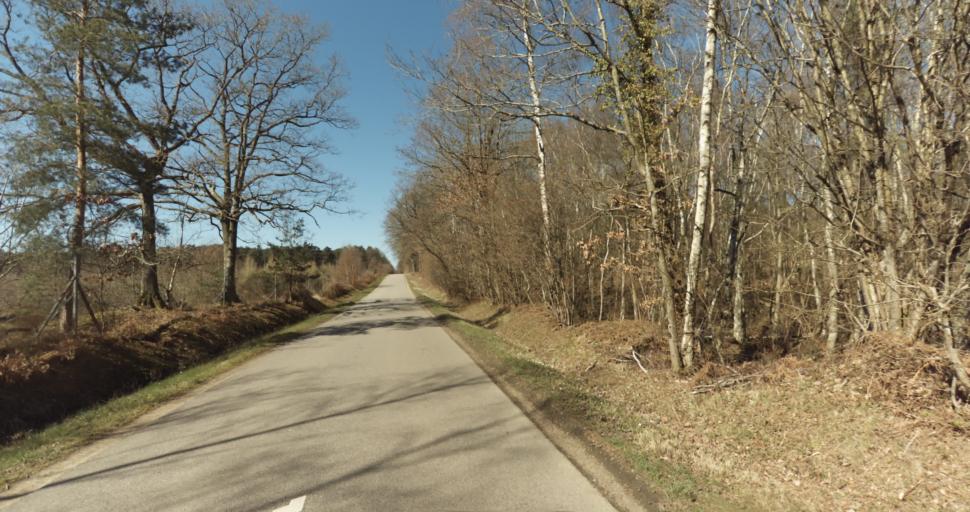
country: FR
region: Lower Normandy
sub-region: Departement du Calvados
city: Livarot
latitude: 48.9660
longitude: 0.0932
